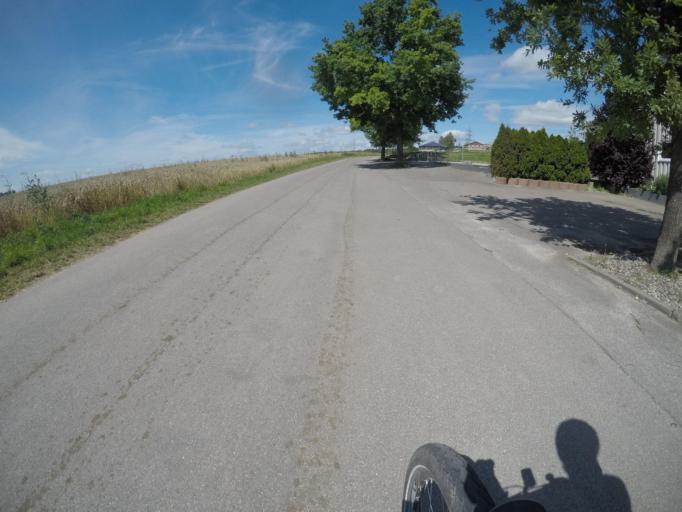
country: DE
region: Baden-Wuerttemberg
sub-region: Regierungsbezirk Stuttgart
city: Ehningen
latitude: 48.6584
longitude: 8.9263
